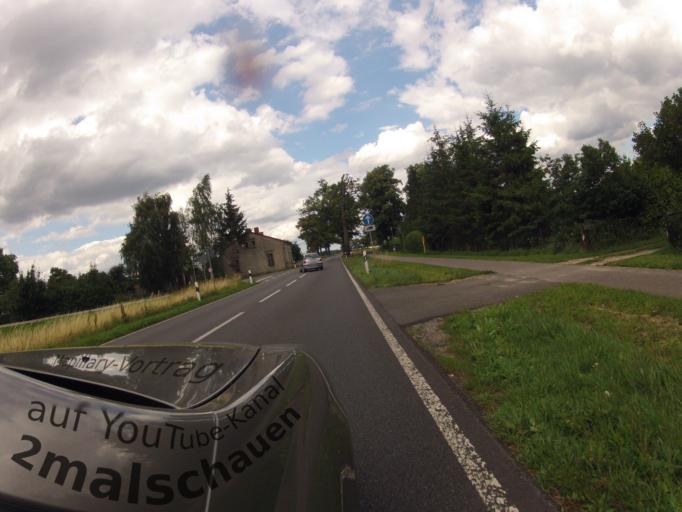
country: DE
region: Mecklenburg-Vorpommern
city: Anklam
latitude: 53.8865
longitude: 13.7043
